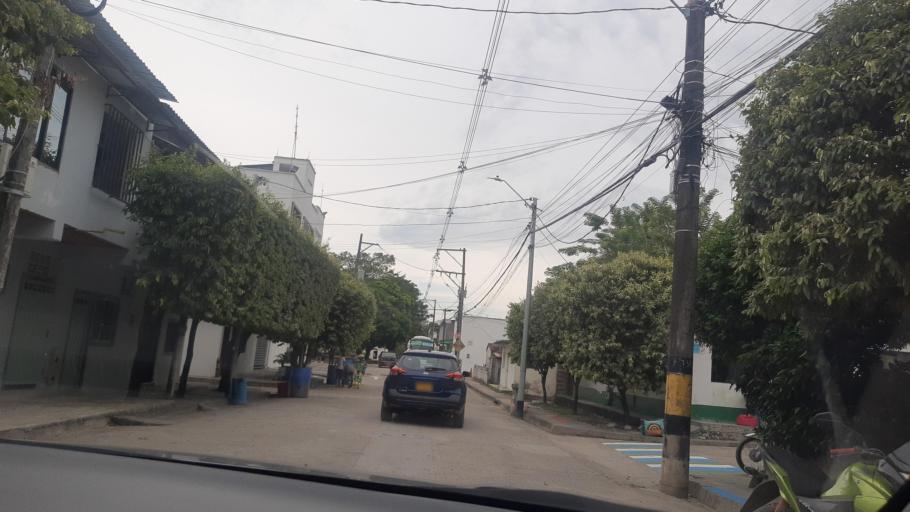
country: CO
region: Antioquia
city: Puerto Triunfo
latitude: 5.8700
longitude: -74.6411
